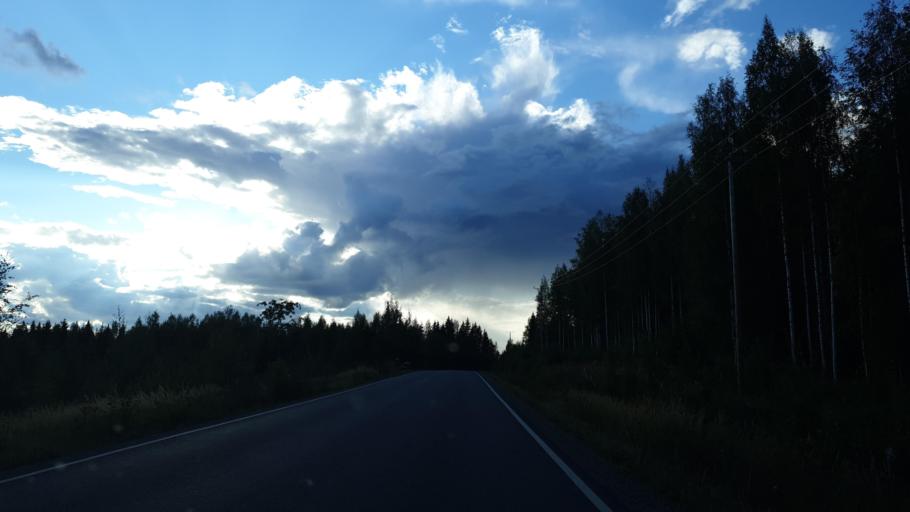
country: FI
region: Northern Savo
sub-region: Koillis-Savo
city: Juankoski
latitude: 63.1888
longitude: 28.3207
